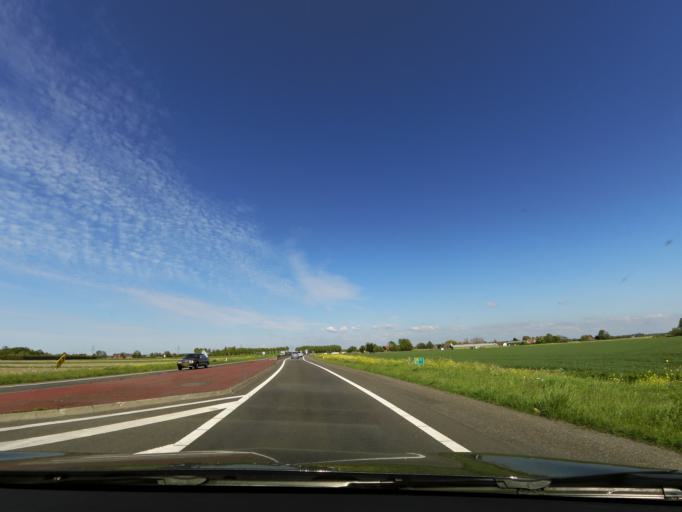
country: NL
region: South Holland
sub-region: Gemeente Hellevoetsluis
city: Nieuwenhoorn
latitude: 51.8619
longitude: 4.1595
